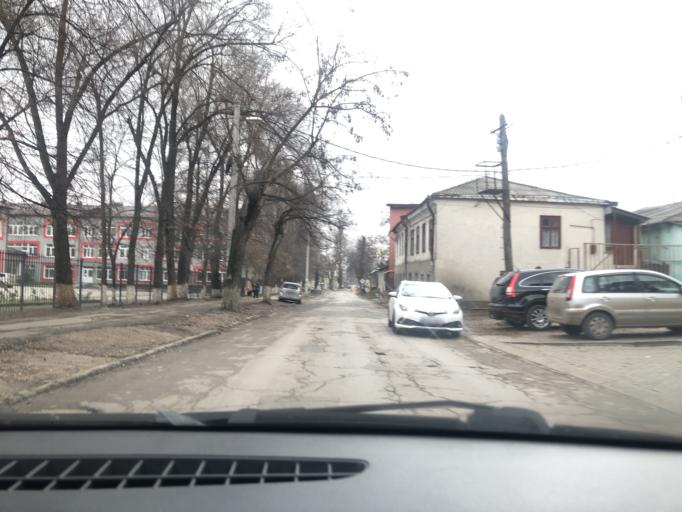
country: MD
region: Chisinau
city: Chisinau
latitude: 47.0236
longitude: 28.8492
